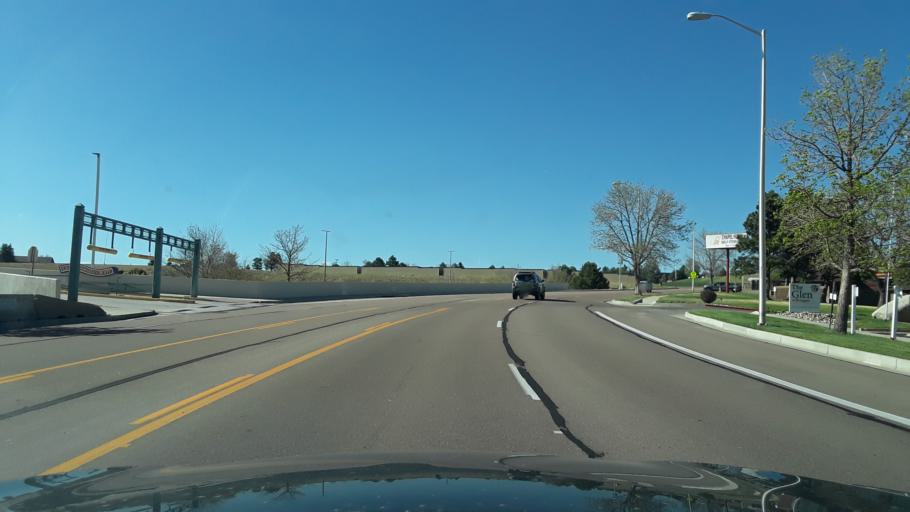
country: US
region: Colorado
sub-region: El Paso County
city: Air Force Academy
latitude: 38.9492
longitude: -104.7920
